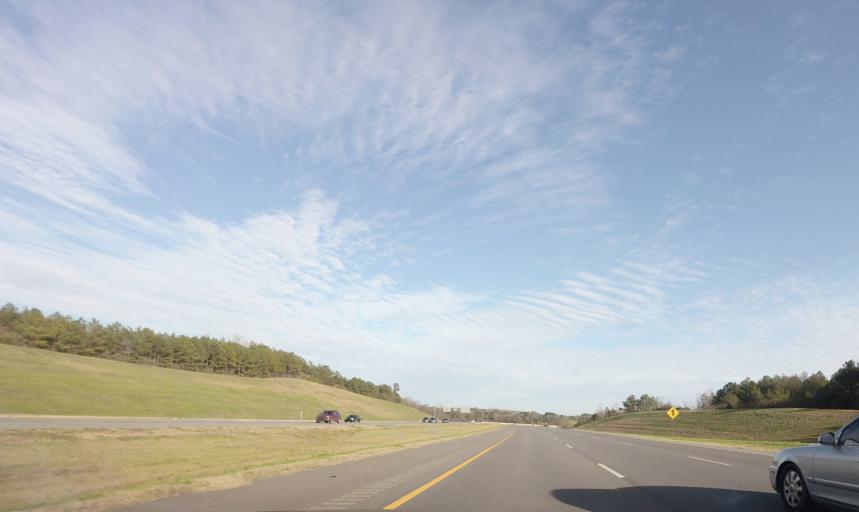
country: US
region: Alabama
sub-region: Walker County
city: Jasper
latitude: 33.8066
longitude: -87.2760
